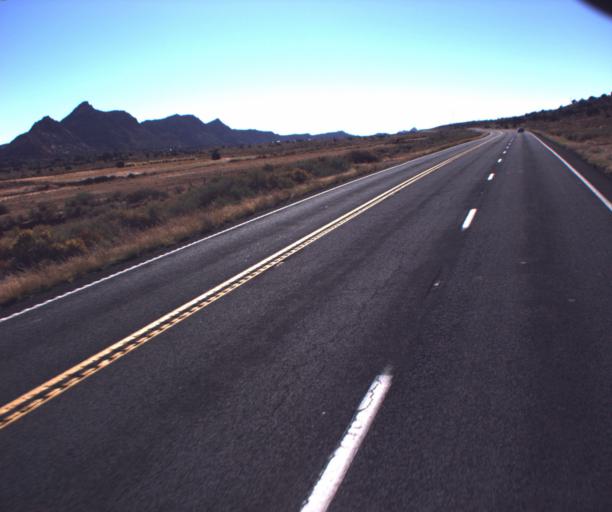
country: US
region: Arizona
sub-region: Coconino County
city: Tuba City
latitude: 36.4095
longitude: -111.5378
